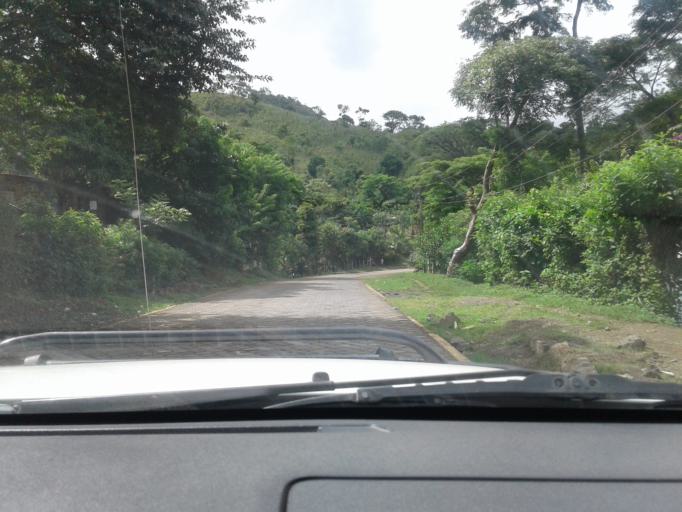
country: NI
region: Matagalpa
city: San Ramon
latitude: 12.9156
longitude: -85.8114
